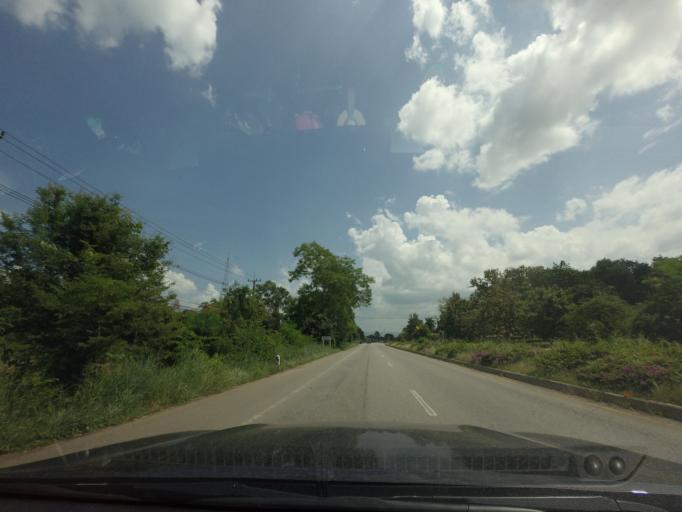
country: TH
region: Phetchabun
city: Phetchabun
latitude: 16.2517
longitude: 101.0663
